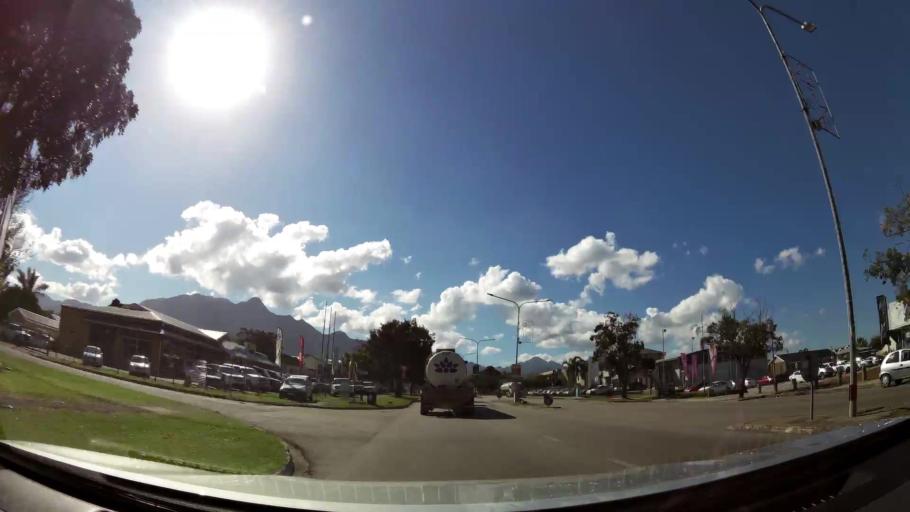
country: ZA
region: Western Cape
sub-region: Eden District Municipality
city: George
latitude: -33.9657
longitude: 22.4513
